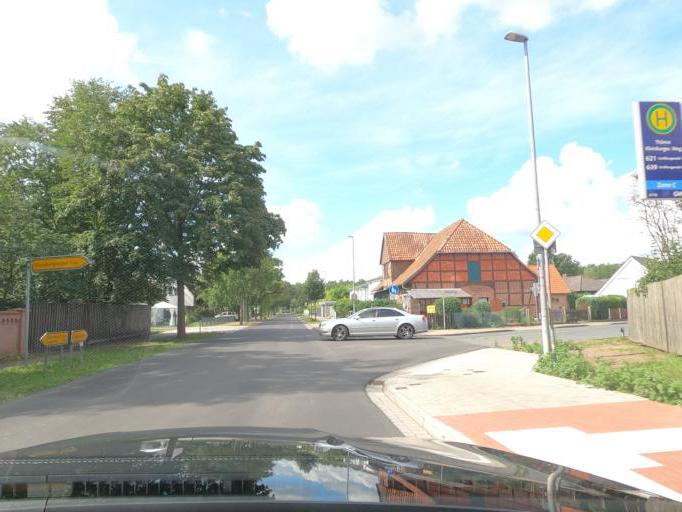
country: DE
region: Lower Saxony
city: Isernhagen Farster Bauerschaft
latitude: 52.4940
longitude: 9.8956
